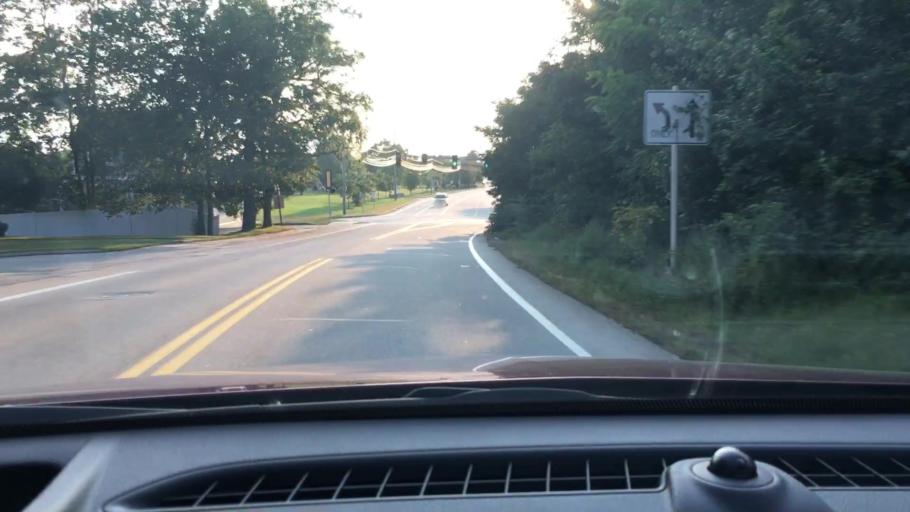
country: US
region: New Hampshire
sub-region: Rockingham County
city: Portsmouth
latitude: 43.0580
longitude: -70.7816
